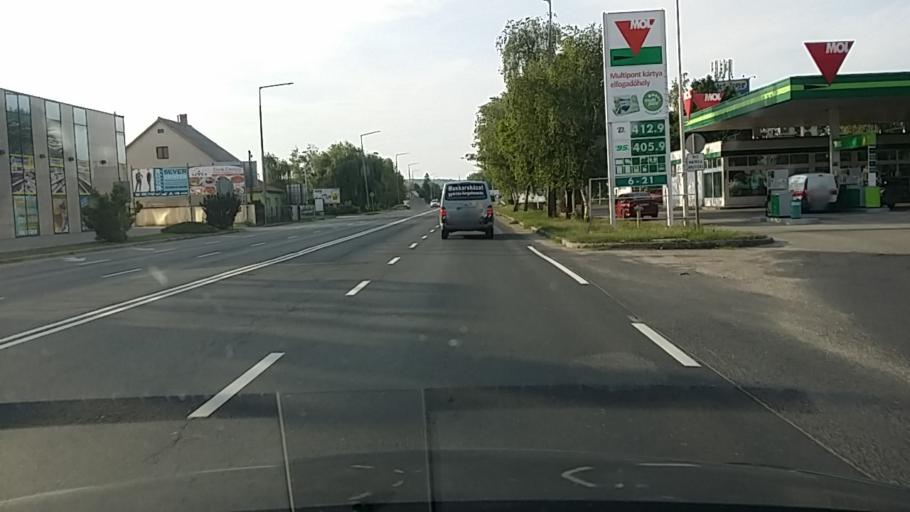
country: HU
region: Borsod-Abauj-Zemplen
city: Miskolc
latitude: 48.0559
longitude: 20.7978
